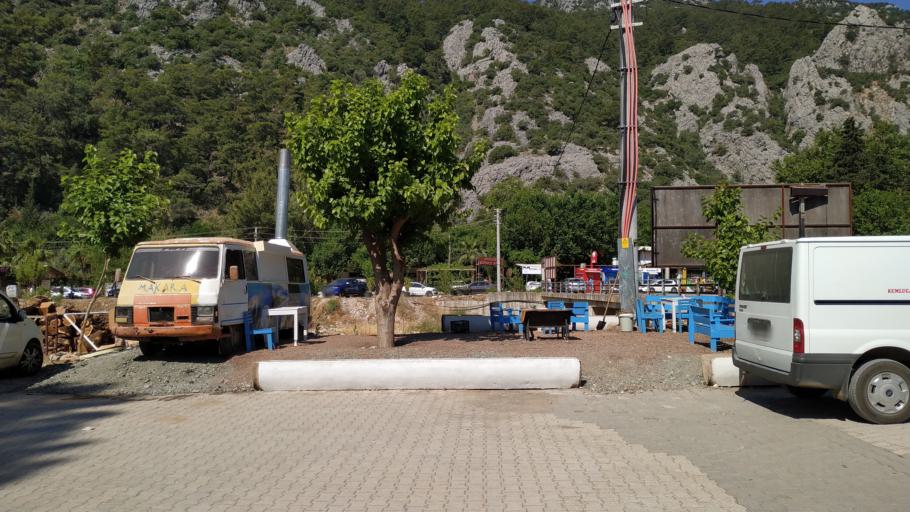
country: TR
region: Antalya
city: Tekirova
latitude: 36.4040
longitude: 30.4734
